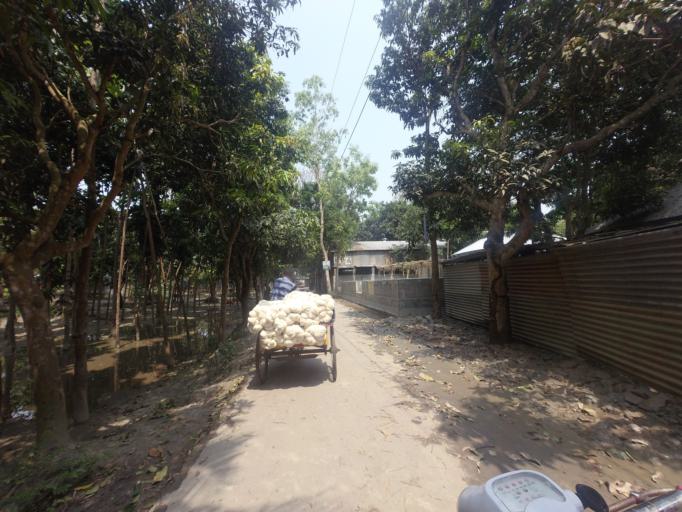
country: BD
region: Rajshahi
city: Sirajganj
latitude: 24.3617
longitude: 89.7175
